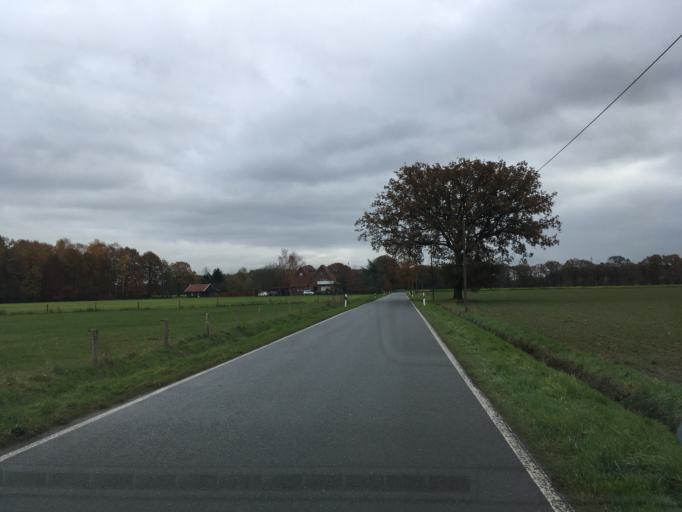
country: DE
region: North Rhine-Westphalia
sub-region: Regierungsbezirk Munster
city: Gescher
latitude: 51.9798
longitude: 6.9952
